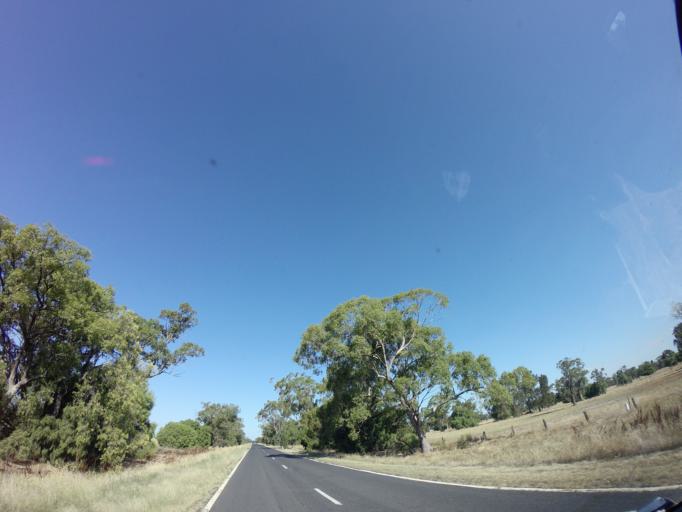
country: AU
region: New South Wales
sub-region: Gilgandra
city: Gilgandra
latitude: -31.6730
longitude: 148.2383
